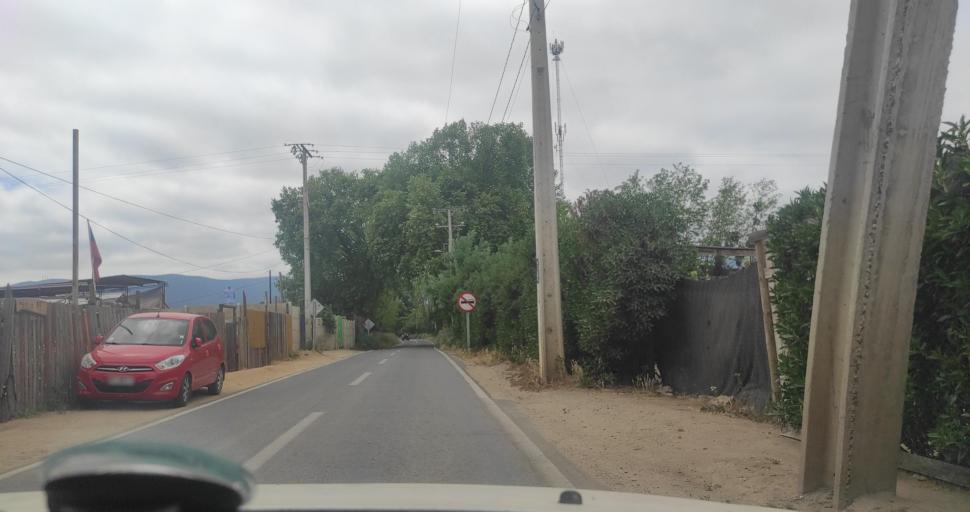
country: CL
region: Valparaiso
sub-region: Provincia de Marga Marga
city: Limache
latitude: -33.0298
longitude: -71.2398
